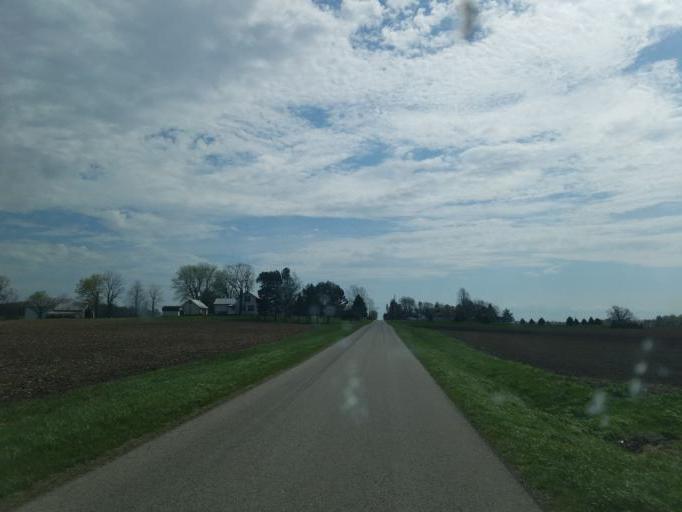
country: US
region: Ohio
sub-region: Crawford County
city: Bucyrus
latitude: 40.7902
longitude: -83.0675
